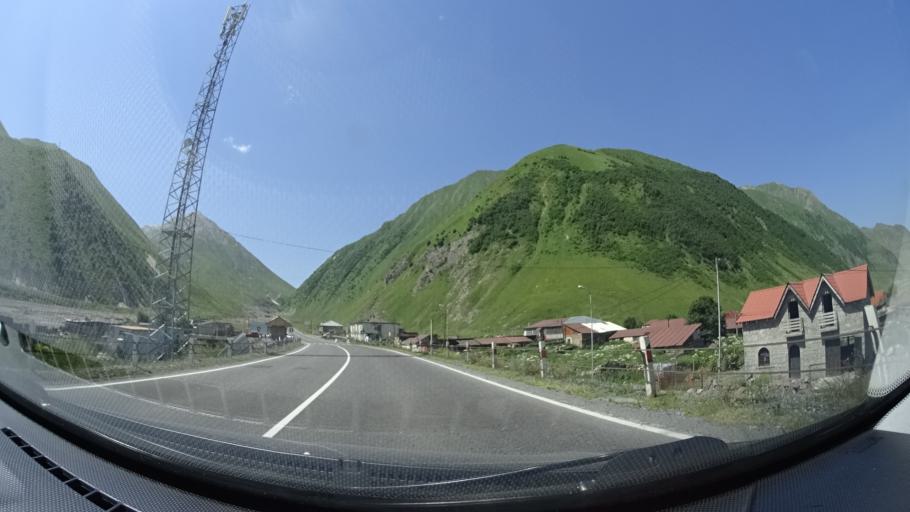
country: GE
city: Gudauri
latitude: 42.5567
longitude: 44.5007
